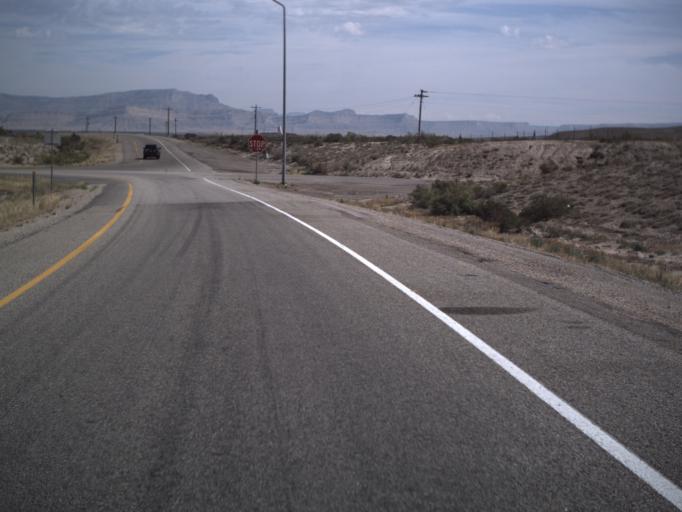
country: US
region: Utah
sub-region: Carbon County
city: East Carbon City
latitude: 38.9898
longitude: -110.1897
